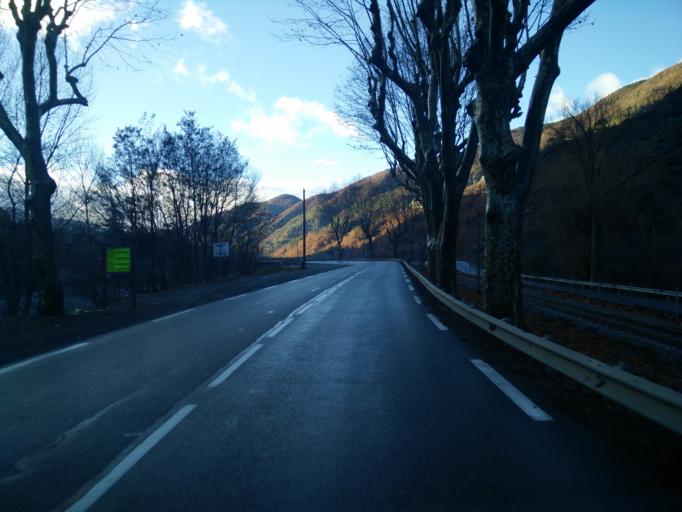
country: FR
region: Provence-Alpes-Cote d'Azur
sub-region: Departement des Alpes-Maritimes
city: Puget-Theniers
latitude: 43.9522
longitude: 6.8791
